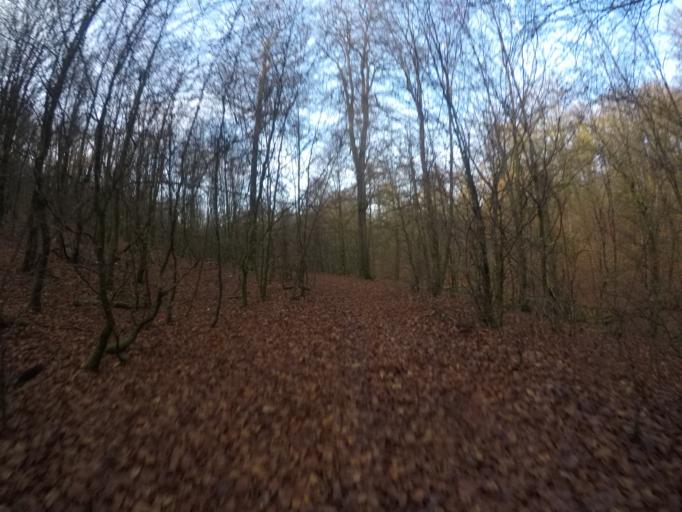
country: BE
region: Wallonia
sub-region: Province du Luxembourg
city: Habay-la-Vieille
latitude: 49.7736
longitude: 5.6577
